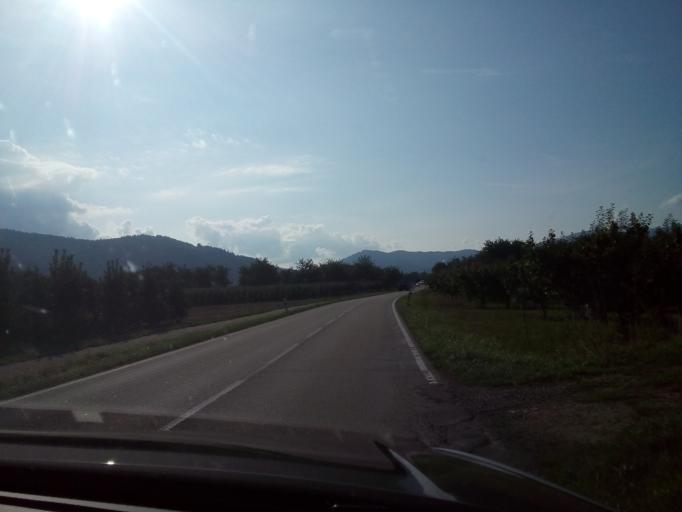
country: DE
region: Baden-Wuerttemberg
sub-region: Freiburg Region
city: Oberkirch
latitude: 48.5460
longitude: 8.0645
